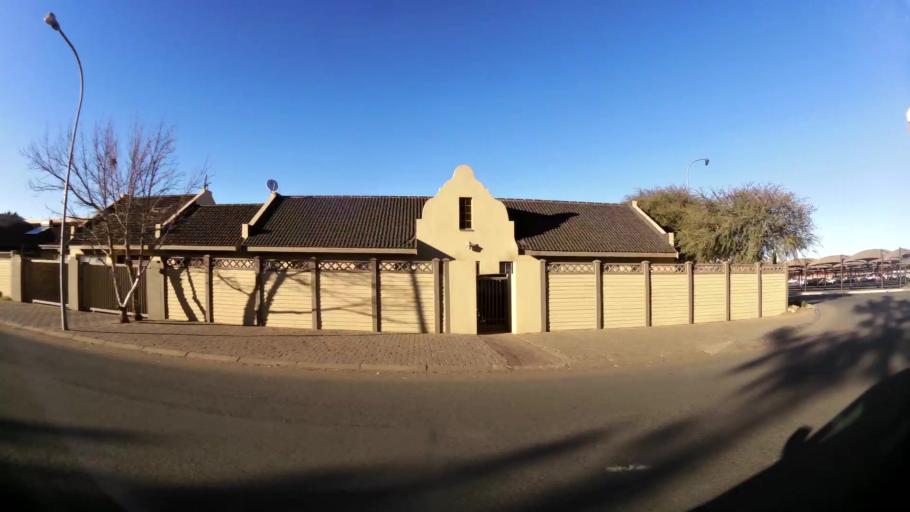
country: ZA
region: Northern Cape
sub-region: Frances Baard District Municipality
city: Kimberley
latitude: -28.7562
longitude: 24.7597
